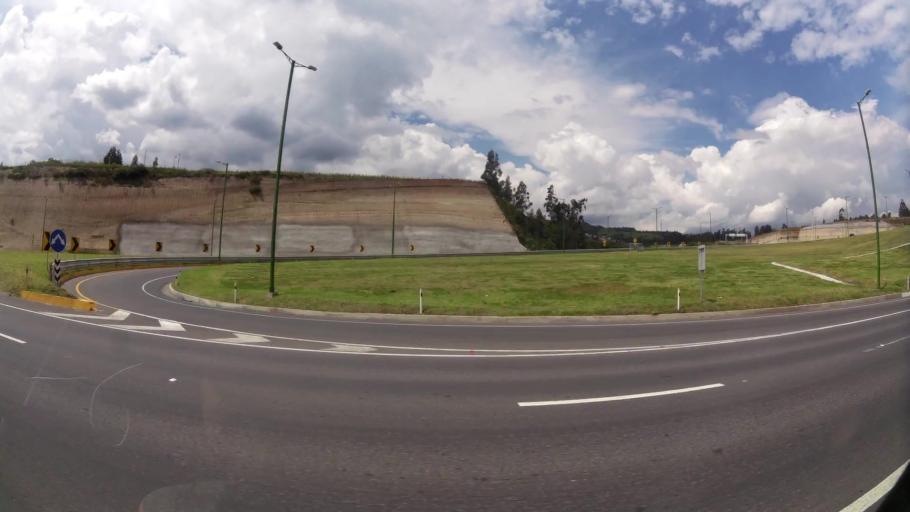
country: EC
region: Pichincha
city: Sangolqui
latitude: -0.2129
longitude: -78.3335
